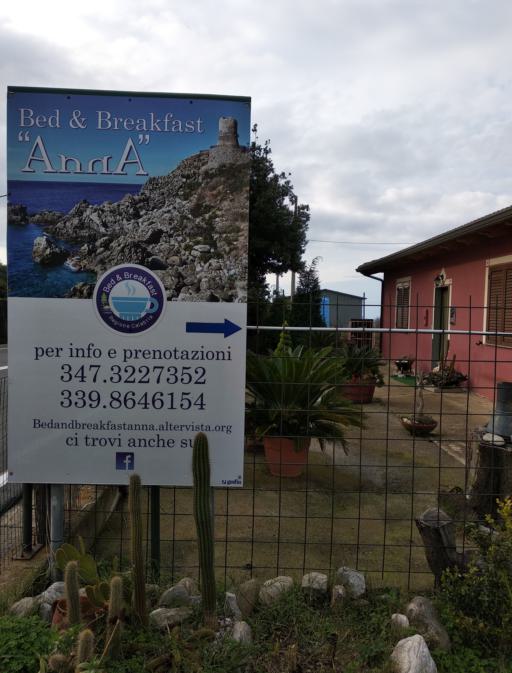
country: IT
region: Calabria
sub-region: Provincia di Reggio Calabria
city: Ceramida-Pellegrina
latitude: 38.3103
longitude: 15.8407
